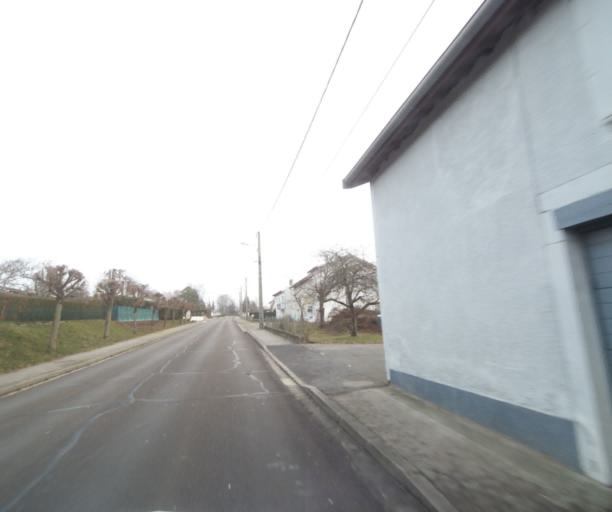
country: FR
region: Champagne-Ardenne
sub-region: Departement de la Haute-Marne
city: Chancenay
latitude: 48.6705
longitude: 4.9884
